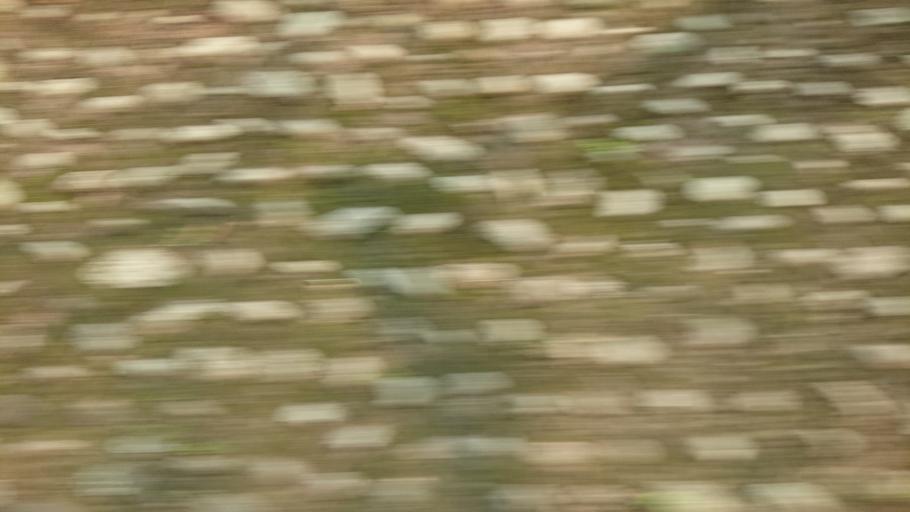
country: TW
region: Taiwan
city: Daxi
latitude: 24.8658
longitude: 121.4192
